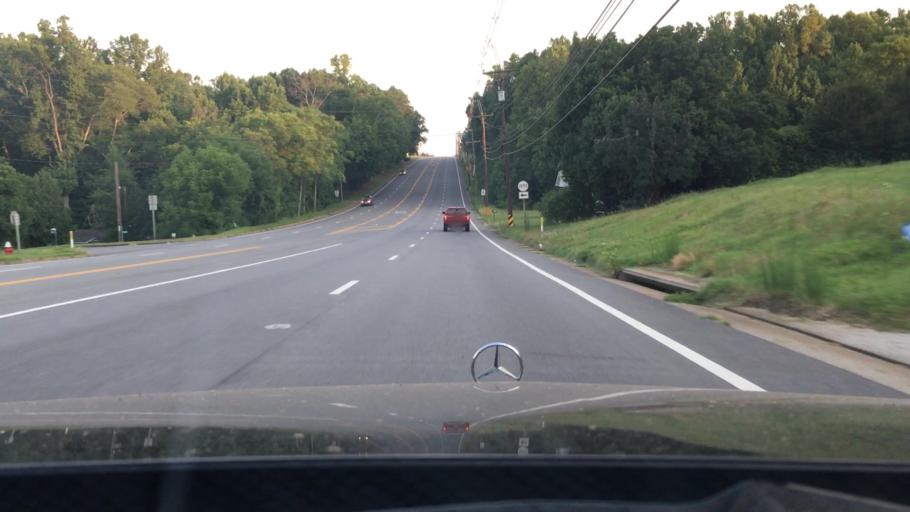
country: US
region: Virginia
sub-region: Pittsylvania County
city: Mount Hermon
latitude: 36.6749
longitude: -79.3745
